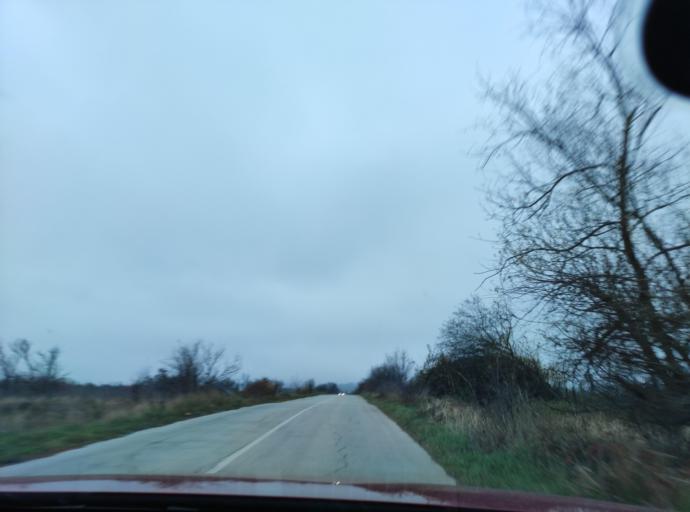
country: BG
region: Lovech
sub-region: Obshtina Yablanitsa
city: Yablanitsa
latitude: 43.0818
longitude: 24.0780
